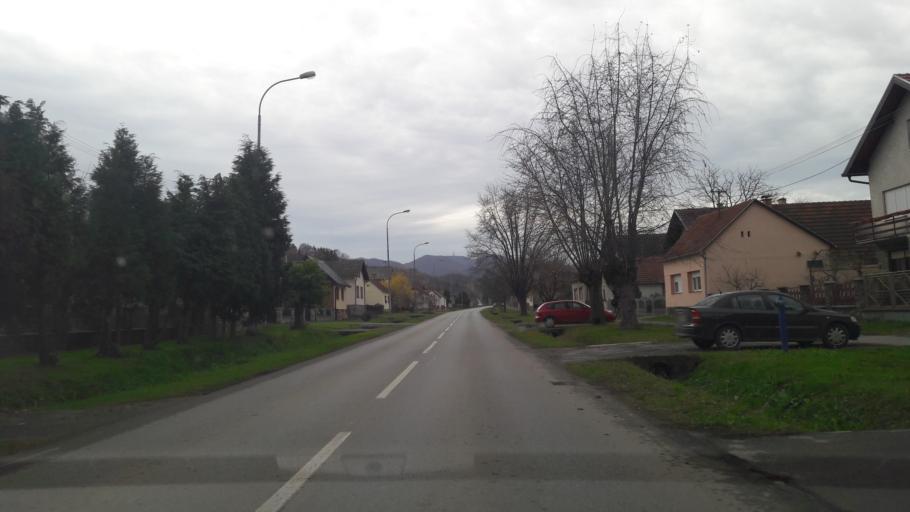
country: HR
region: Virovitick-Podravska
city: Orahovica
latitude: 45.5441
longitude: 17.8994
